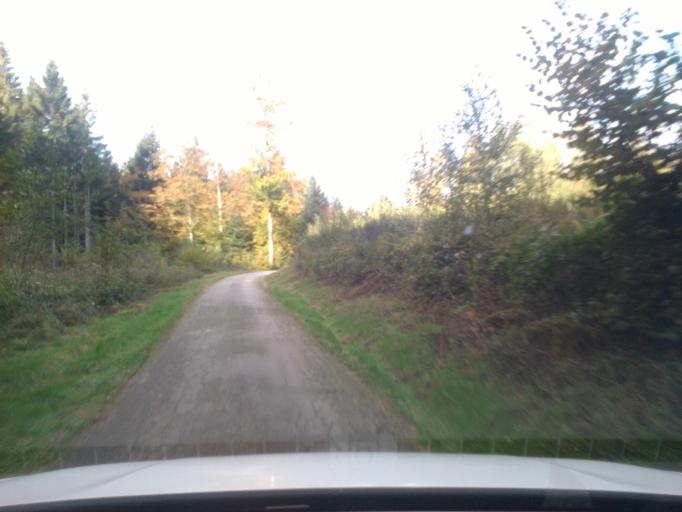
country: FR
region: Lorraine
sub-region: Departement des Vosges
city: Senones
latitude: 48.3936
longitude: 7.0679
